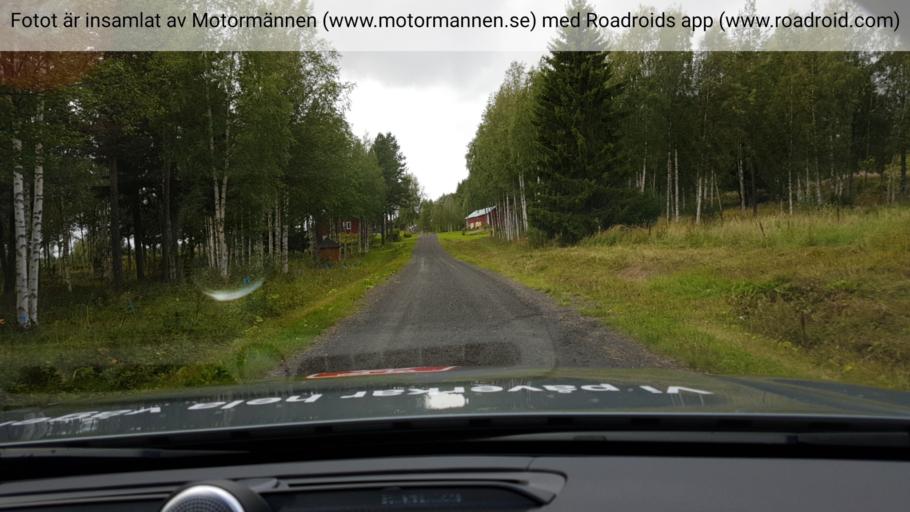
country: SE
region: Jaemtland
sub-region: OEstersunds Kommun
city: Lit
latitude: 63.7755
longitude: 14.6466
